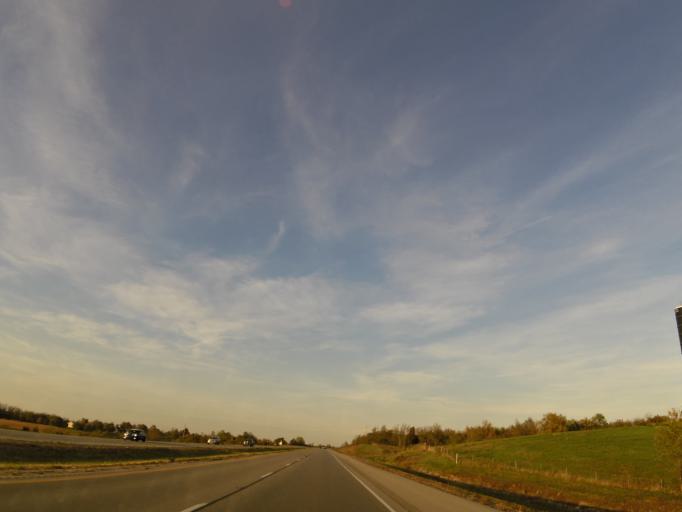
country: US
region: Kentucky
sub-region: Garrard County
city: Lancaster
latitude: 37.7173
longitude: -84.6447
